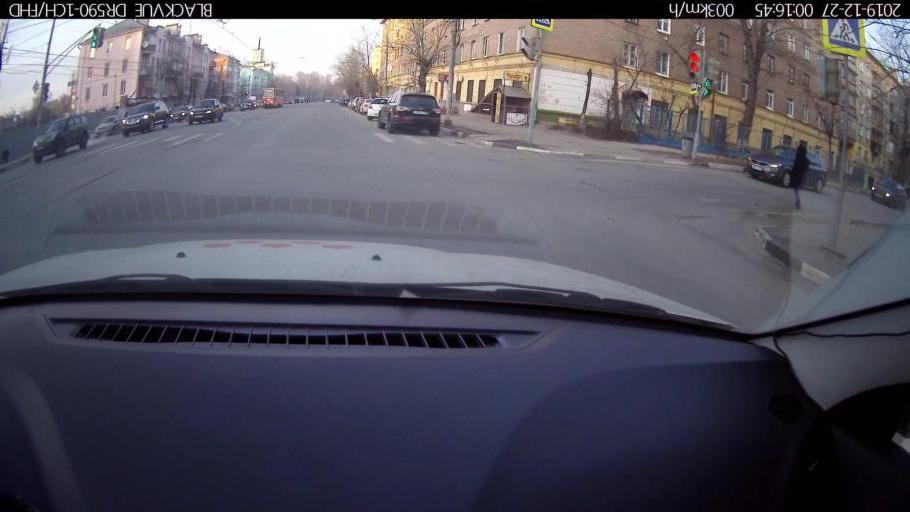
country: RU
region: Nizjnij Novgorod
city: Nizhniy Novgorod
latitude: 56.3049
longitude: 43.9376
